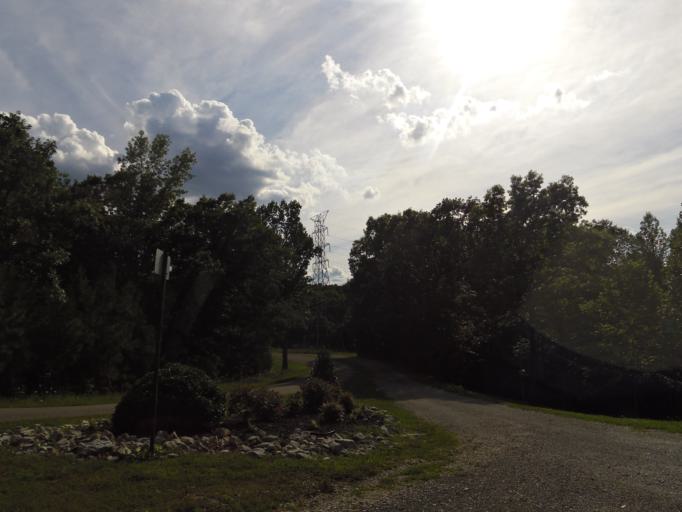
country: US
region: Tennessee
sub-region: Benton County
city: Camden
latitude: 36.0606
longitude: -88.1612
